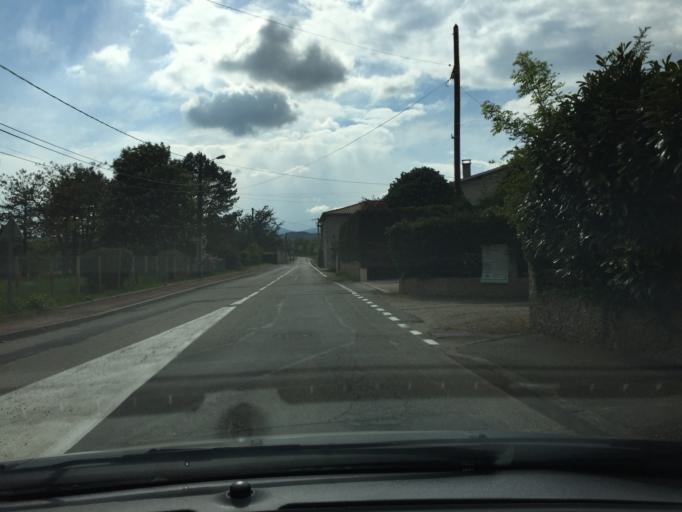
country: FR
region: Rhone-Alpes
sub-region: Departement du Rhone
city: Orlienas
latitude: 45.6563
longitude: 4.7144
